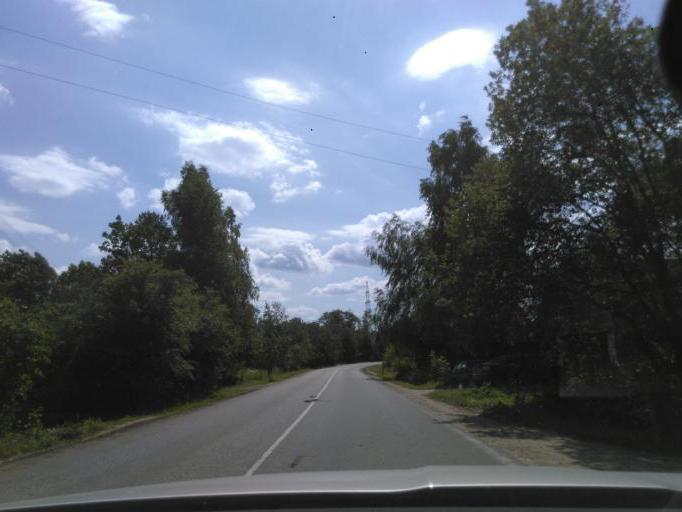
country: RU
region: Moskovskaya
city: Solnechnogorsk
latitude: 56.1635
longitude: 36.9764
